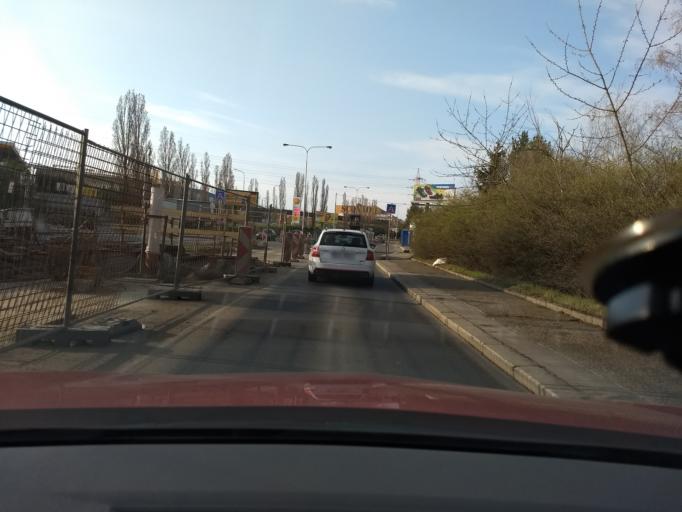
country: CZ
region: Central Bohemia
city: Hostivice
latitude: 50.0590
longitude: 14.3112
